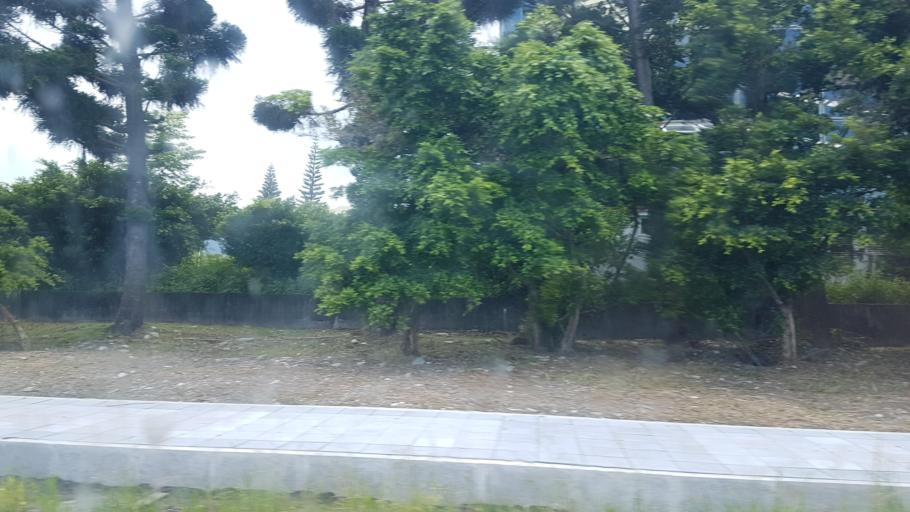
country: TW
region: Taiwan
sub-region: Hualien
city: Hualian
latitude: 23.9276
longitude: 121.5919
